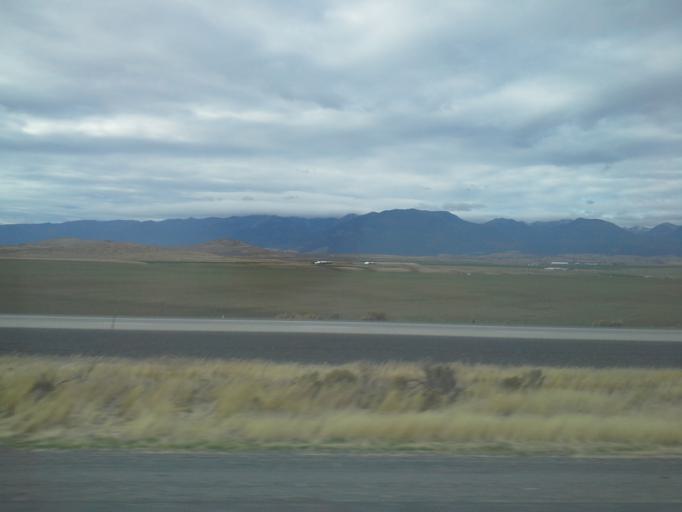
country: US
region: Oregon
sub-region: Baker County
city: Baker City
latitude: 44.9614
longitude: -117.8645
